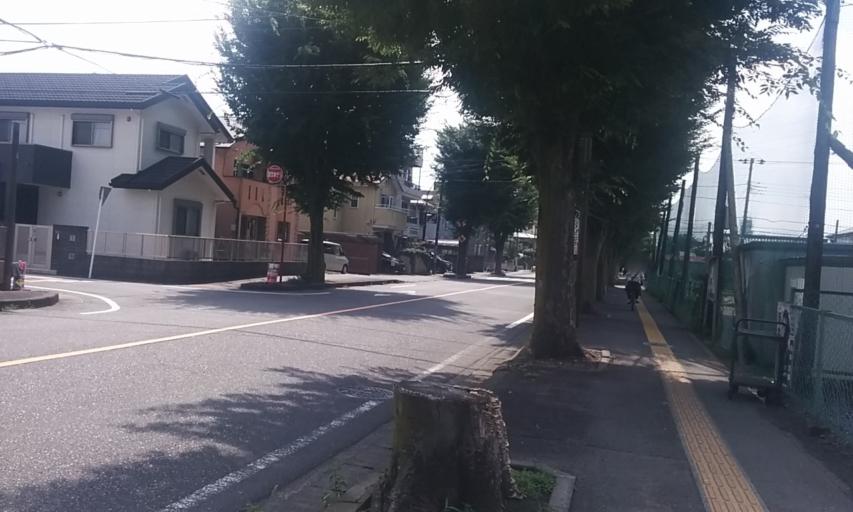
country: JP
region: Tokyo
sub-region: Machida-shi
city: Machida
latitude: 35.5641
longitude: 139.3974
